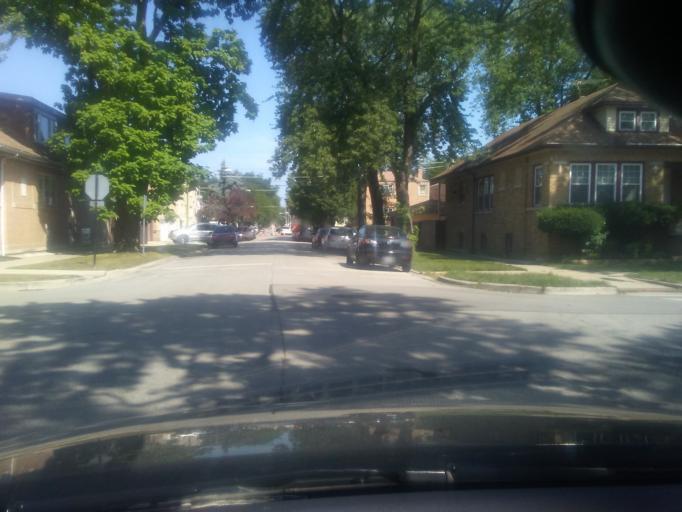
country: US
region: Illinois
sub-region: Cook County
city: Harwood Heights
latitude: 41.9811
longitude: -87.7696
